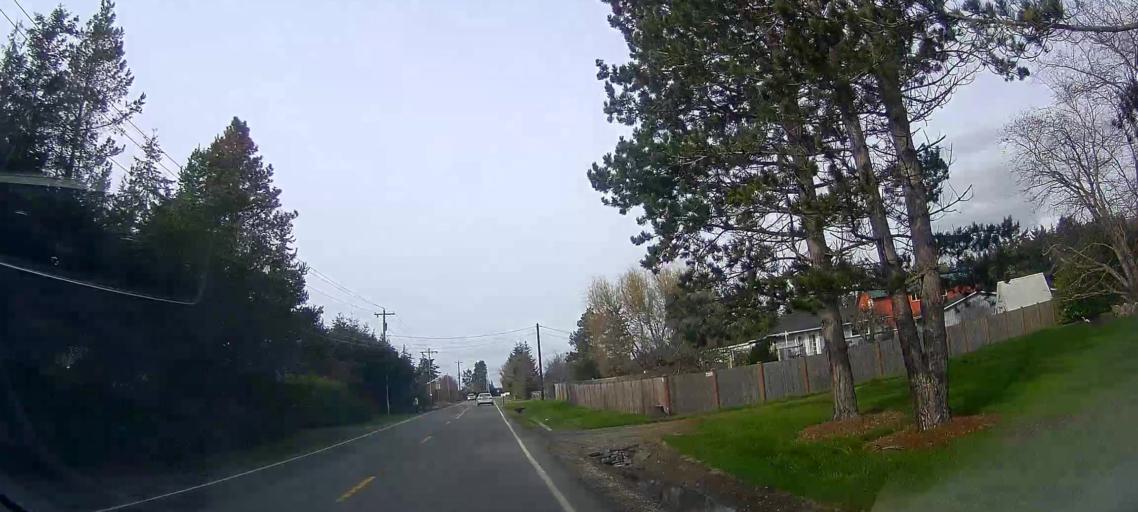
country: US
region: Washington
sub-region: Island County
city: Camano
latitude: 48.1699
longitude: -122.5264
